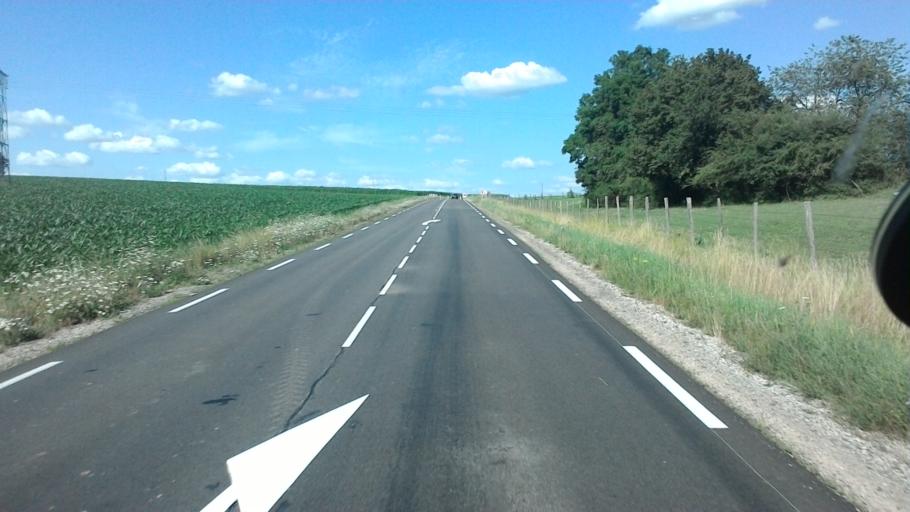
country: FR
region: Franche-Comte
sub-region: Departement de la Haute-Saone
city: Gy
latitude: 47.3808
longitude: 5.7740
